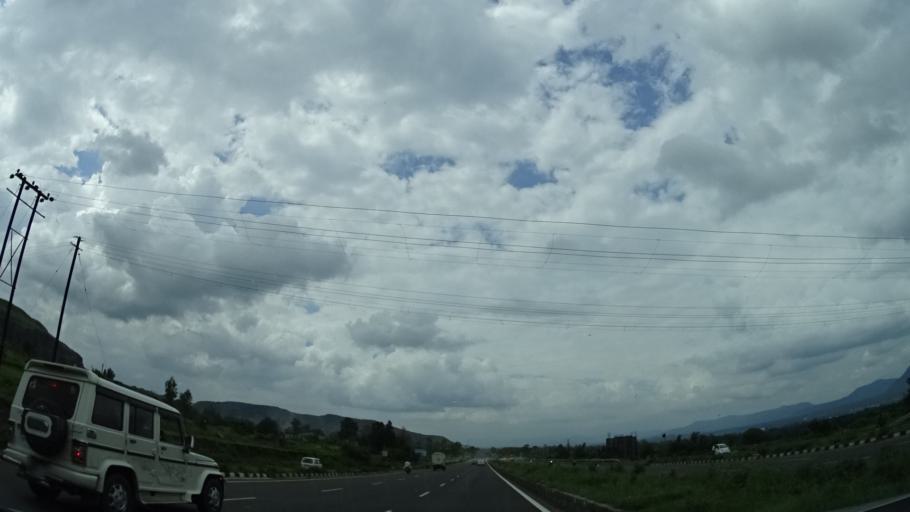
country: IN
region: Maharashtra
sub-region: Satara Division
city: Satara
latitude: 17.7587
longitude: 73.9924
